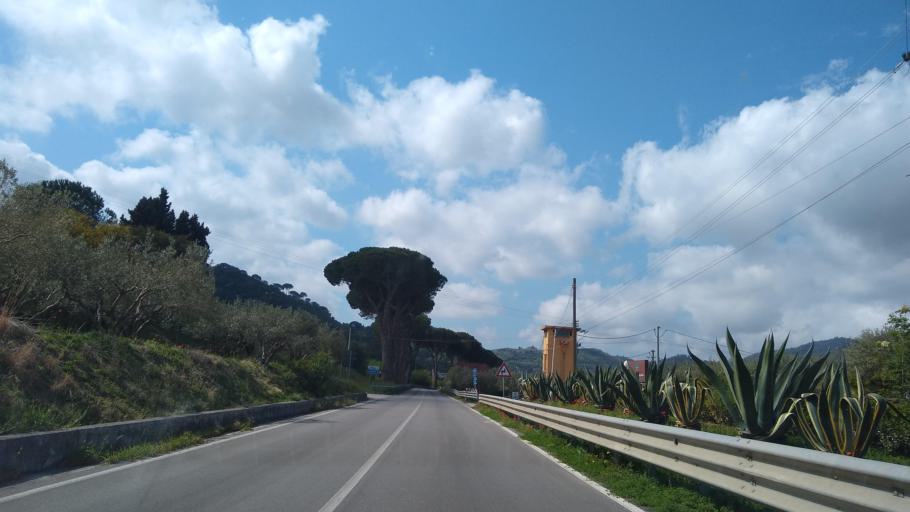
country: IT
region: Sicily
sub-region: Trapani
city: Calatafimi
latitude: 37.9393
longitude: 12.8553
